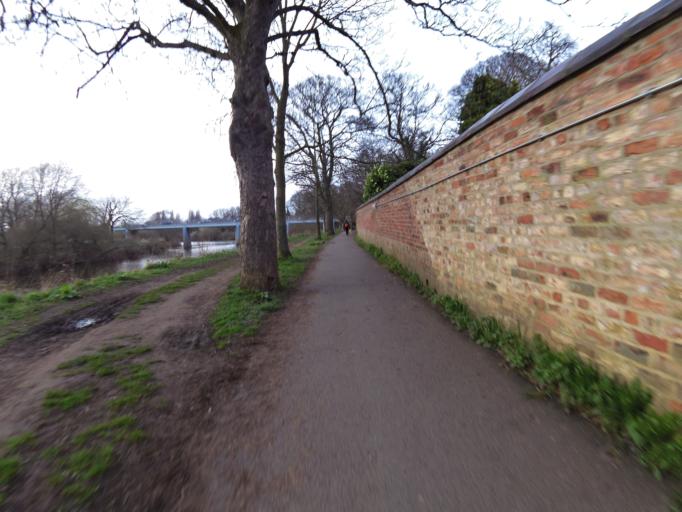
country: GB
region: England
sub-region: City of York
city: York
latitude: 53.9668
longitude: -1.1027
